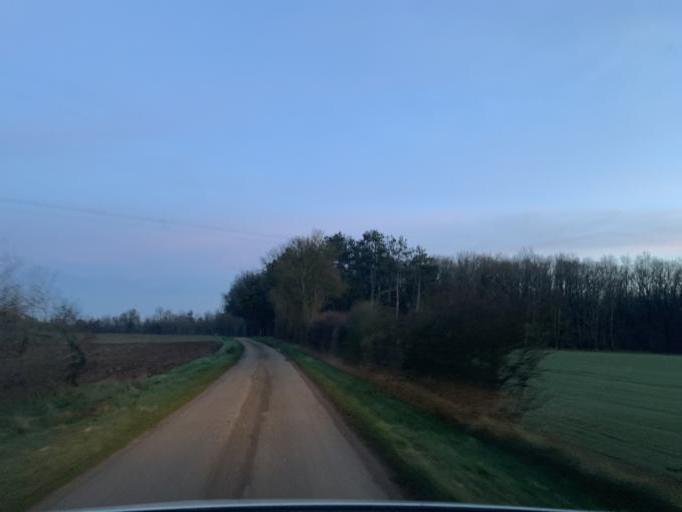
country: FR
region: Bourgogne
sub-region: Departement de l'Yonne
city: Fontenailles
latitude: 47.5576
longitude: 3.3575
